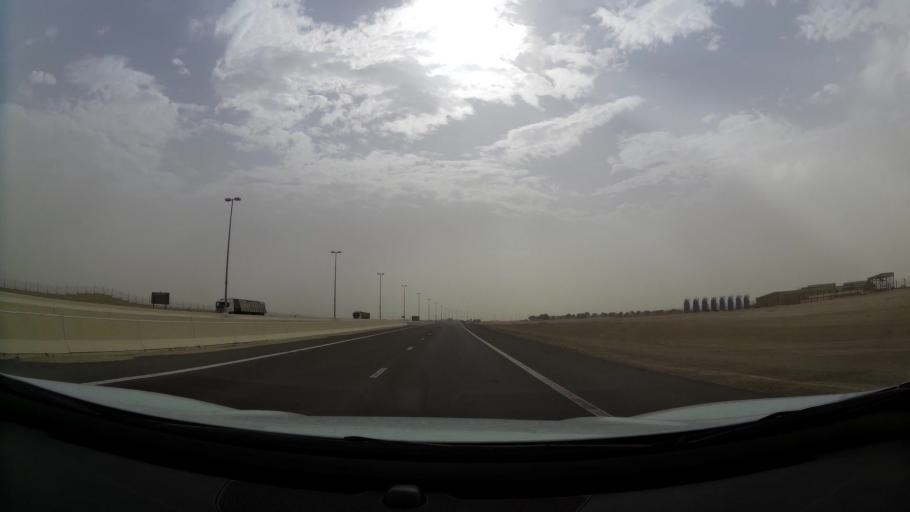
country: AE
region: Abu Dhabi
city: Abu Dhabi
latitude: 24.4779
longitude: 54.6640
